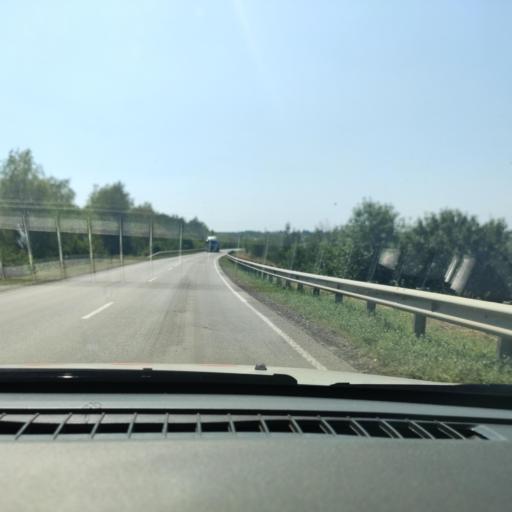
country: RU
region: Voronezj
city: Imeni Pervogo Maya
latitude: 50.7622
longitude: 39.3900
